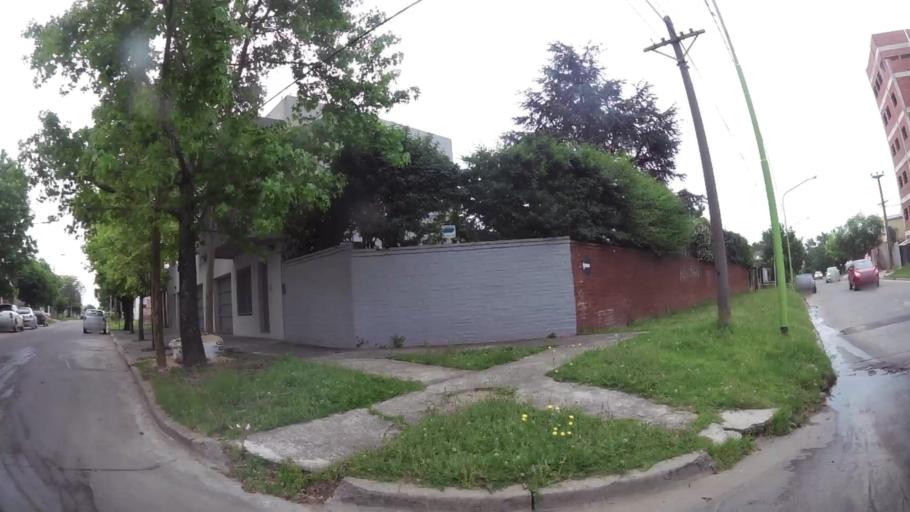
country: AR
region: Buenos Aires
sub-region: Partido de Campana
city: Campana
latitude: -34.1747
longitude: -58.9580
